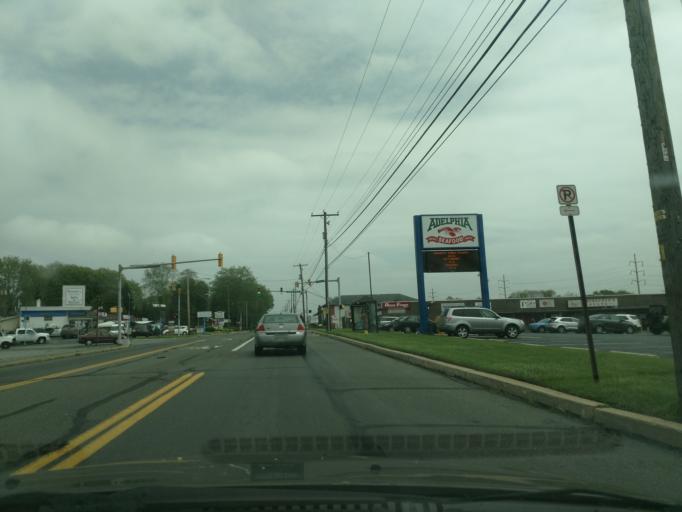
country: US
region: Pennsylvania
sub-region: Berks County
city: Sinking Spring
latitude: 40.3256
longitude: -76.0085
